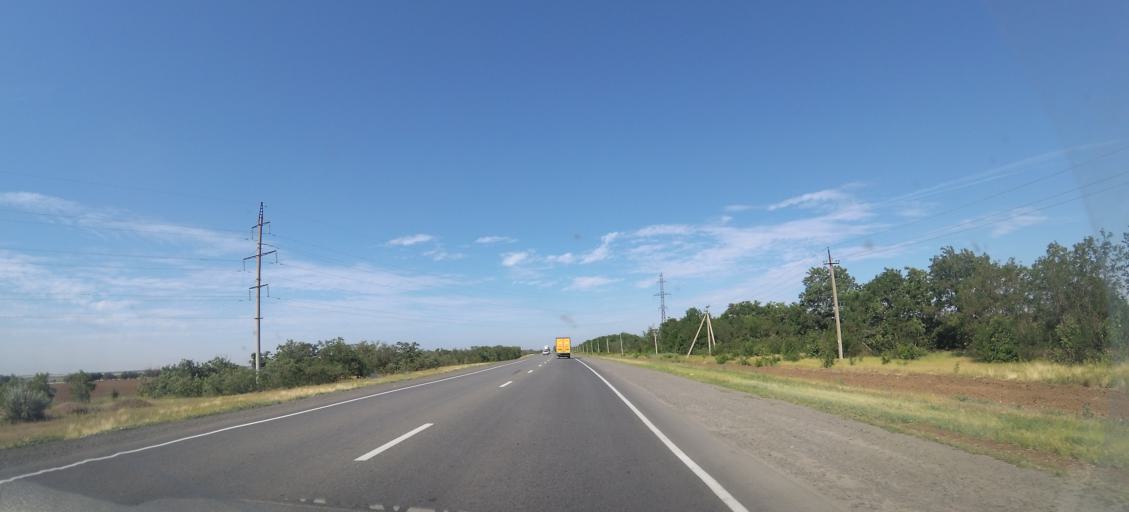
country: RU
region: Volgograd
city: Oktyabr'skiy
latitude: 48.6976
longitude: 43.8023
